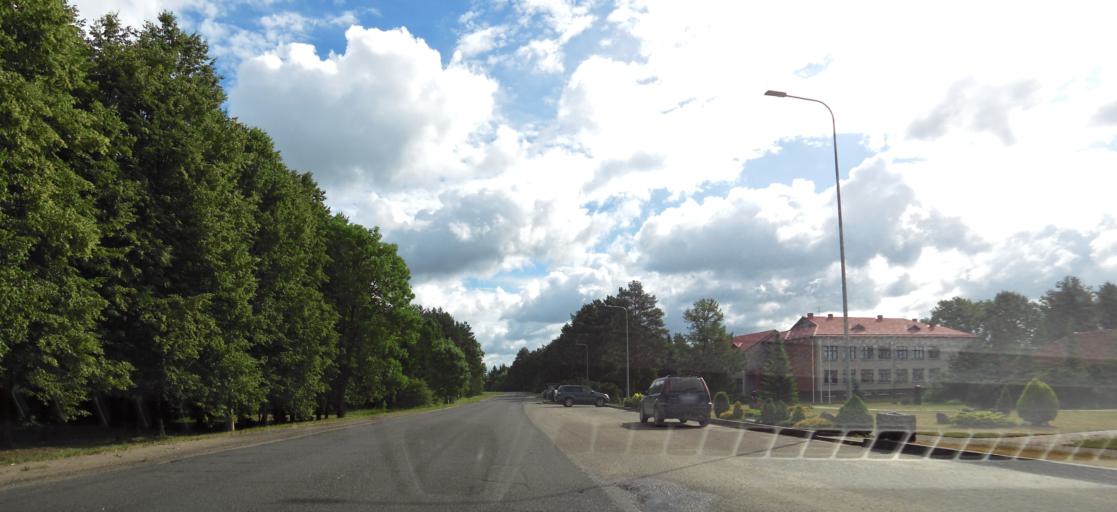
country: LT
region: Panevezys
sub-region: Birzai
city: Birzai
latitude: 56.2103
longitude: 24.7769
